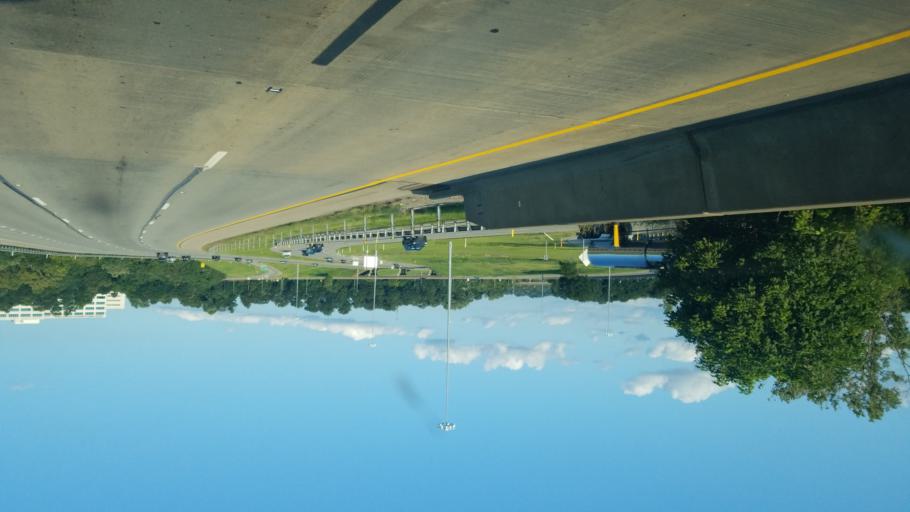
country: US
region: Pennsylvania
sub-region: Allegheny County
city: Bridgeville
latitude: 40.3722
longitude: -80.1094
